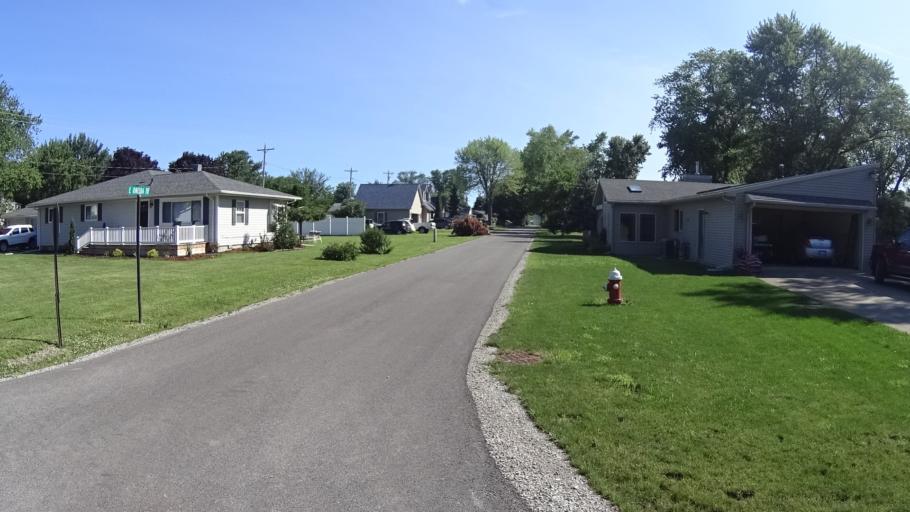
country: US
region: Ohio
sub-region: Erie County
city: Sandusky
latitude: 41.4667
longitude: -82.8244
